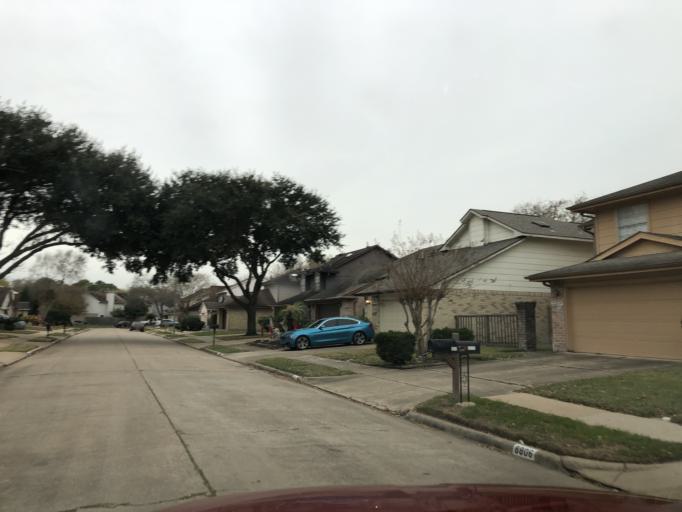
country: US
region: Texas
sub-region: Fort Bend County
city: Missouri City
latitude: 29.6425
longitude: -95.5322
